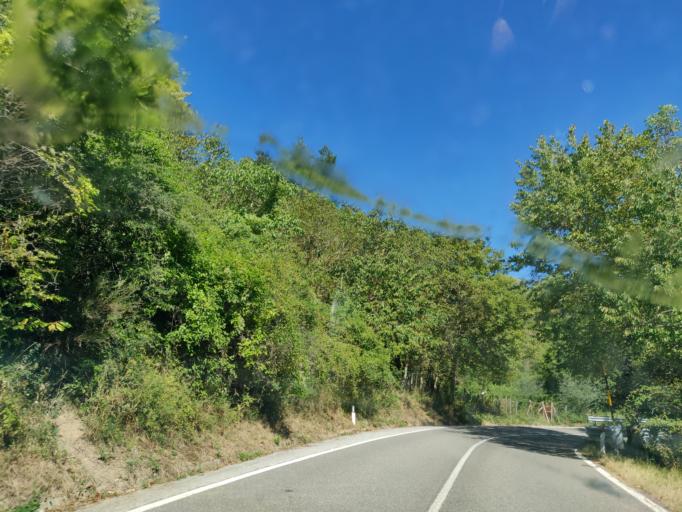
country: IT
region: Tuscany
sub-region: Provincia di Siena
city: Abbadia San Salvatore
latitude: 42.8924
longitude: 11.6572
